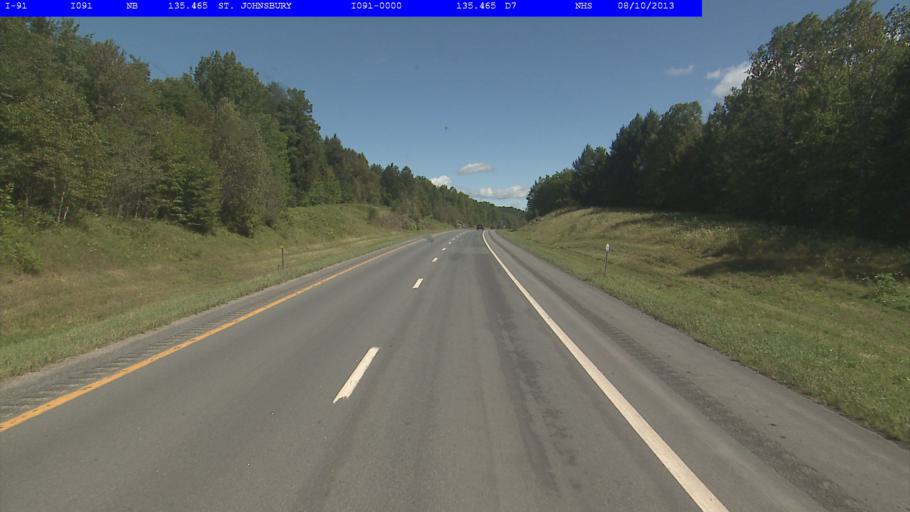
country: US
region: Vermont
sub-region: Caledonia County
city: Lyndon
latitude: 44.4953
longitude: -72.0211
